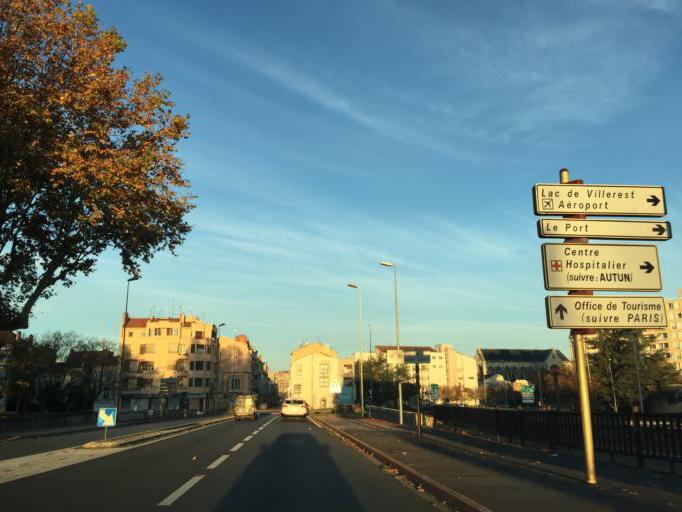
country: FR
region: Rhone-Alpes
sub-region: Departement de la Loire
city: Le Coteau
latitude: 46.0330
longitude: 4.0790
